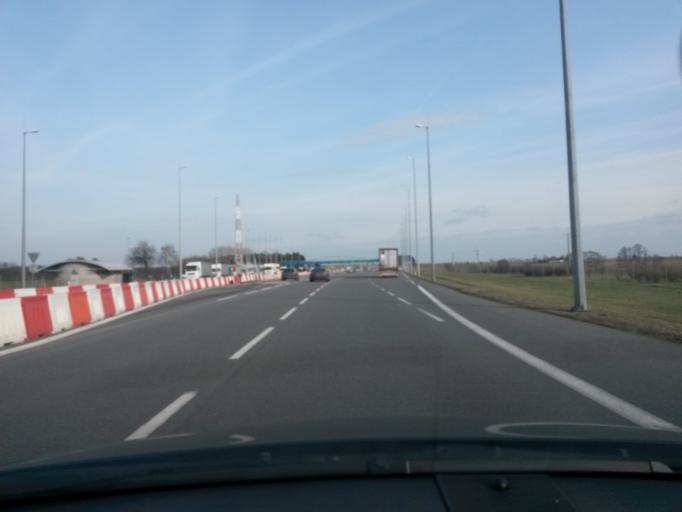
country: PL
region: Greater Poland Voivodeship
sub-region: Powiat slupecki
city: Ladek
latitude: 52.2229
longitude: 17.9468
